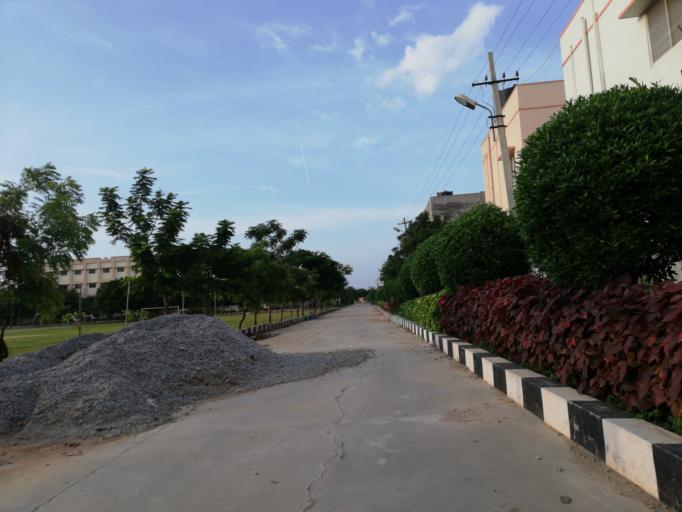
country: IN
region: Telangana
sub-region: Rangareddi
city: Quthbullapur
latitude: 17.5946
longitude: 78.4430
